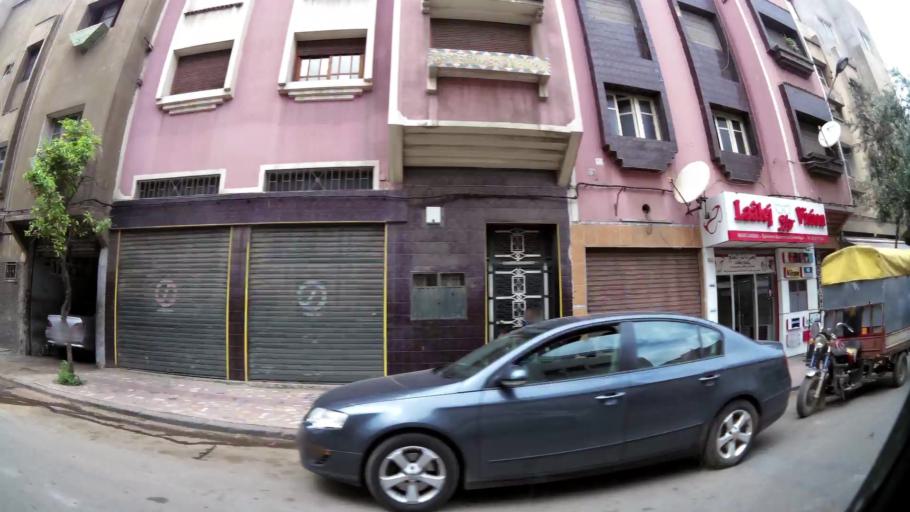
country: MA
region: Grand Casablanca
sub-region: Mediouna
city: Tit Mellil
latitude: 33.5781
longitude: -7.5444
